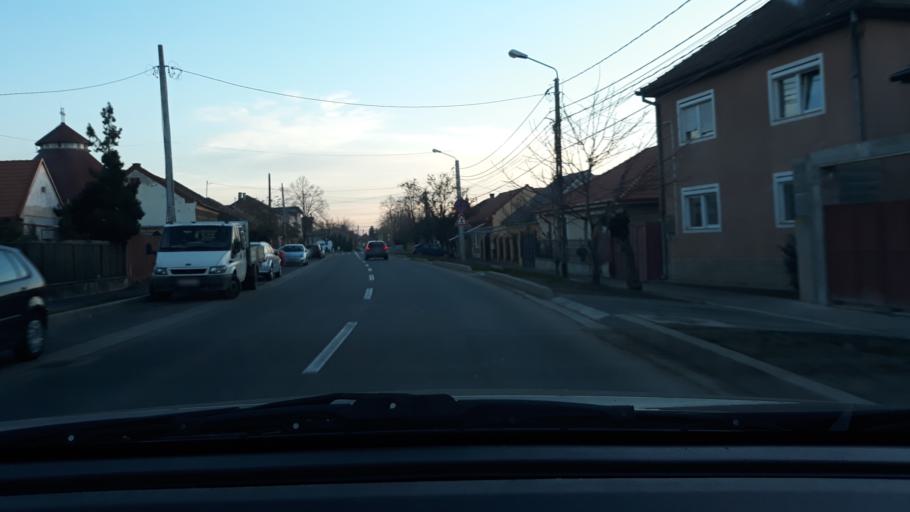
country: RO
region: Bihor
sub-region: Comuna Biharea
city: Oradea
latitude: 47.0866
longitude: 21.9267
